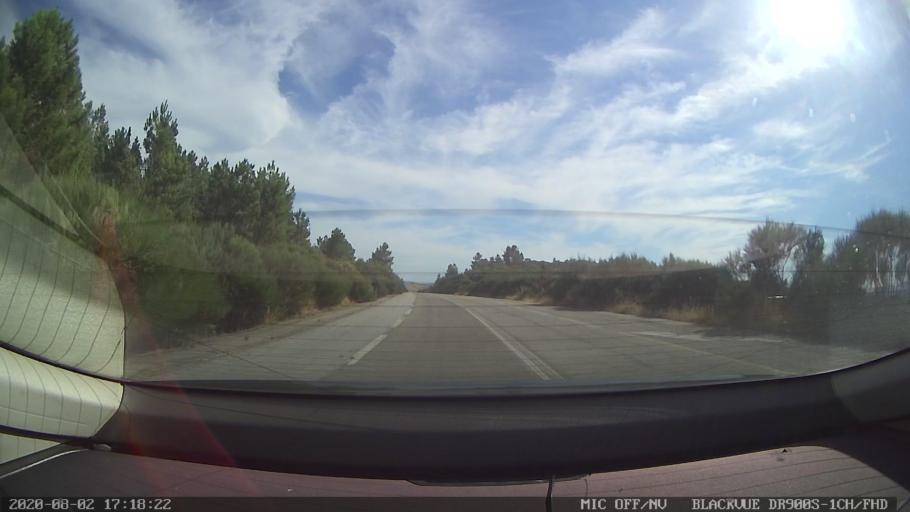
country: PT
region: Vila Real
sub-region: Murca
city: Murca
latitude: 41.3723
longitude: -7.5510
